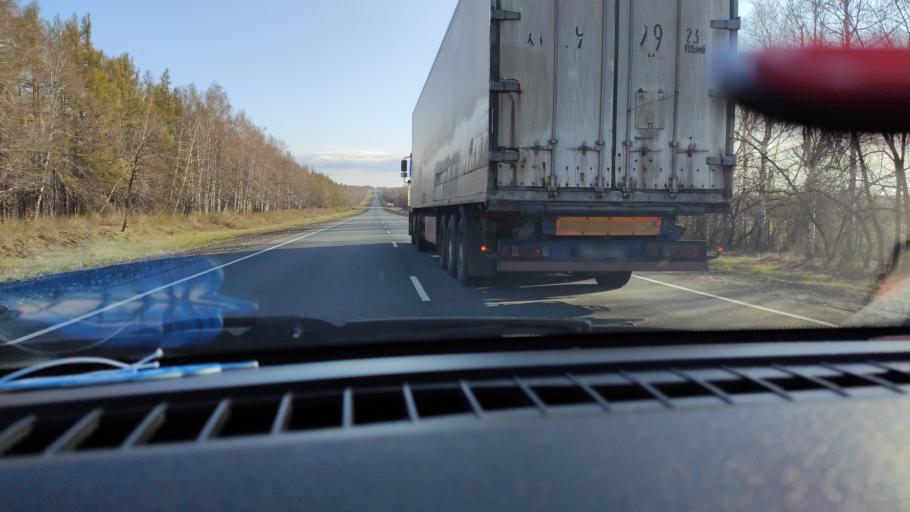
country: RU
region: Saratov
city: Khvalynsk
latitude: 52.5717
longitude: 48.1036
